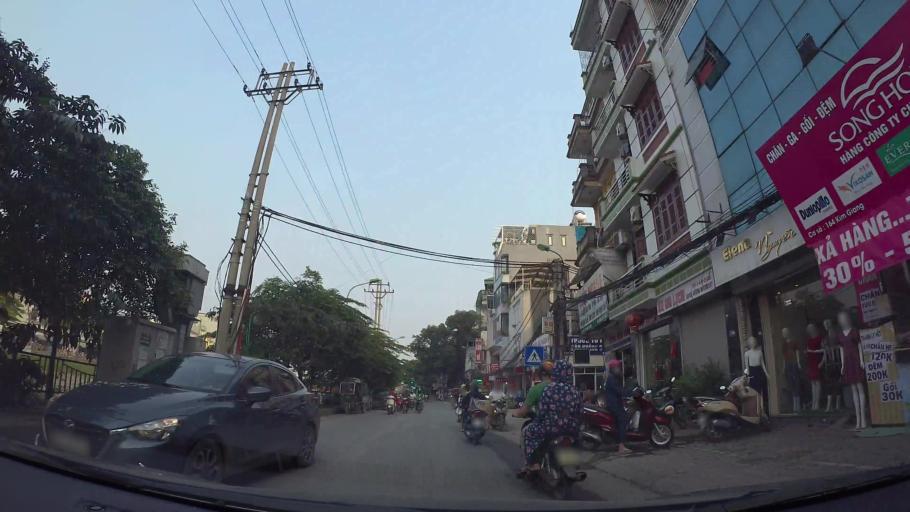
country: VN
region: Ha Noi
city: Thanh Xuan
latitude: 20.9806
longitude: 105.8181
